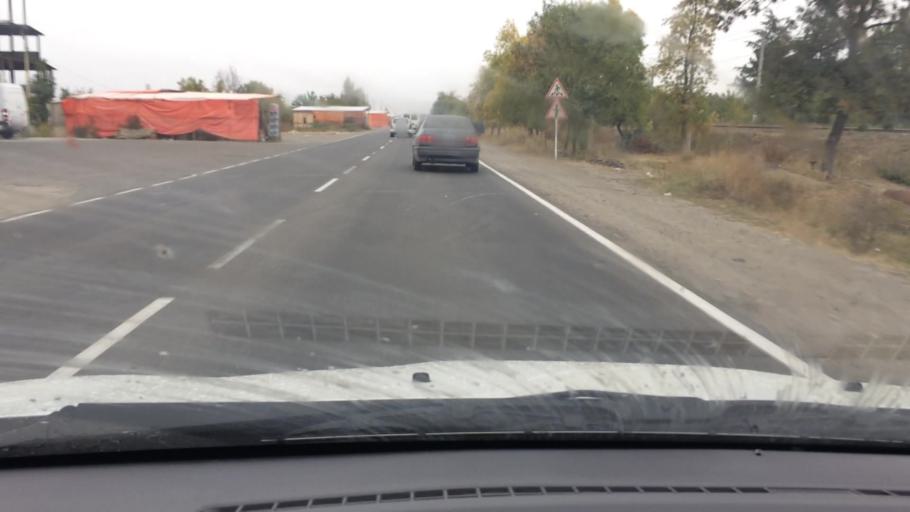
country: GE
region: Kvemo Kartli
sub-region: Marneuli
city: Marneuli
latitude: 41.4187
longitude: 44.8257
